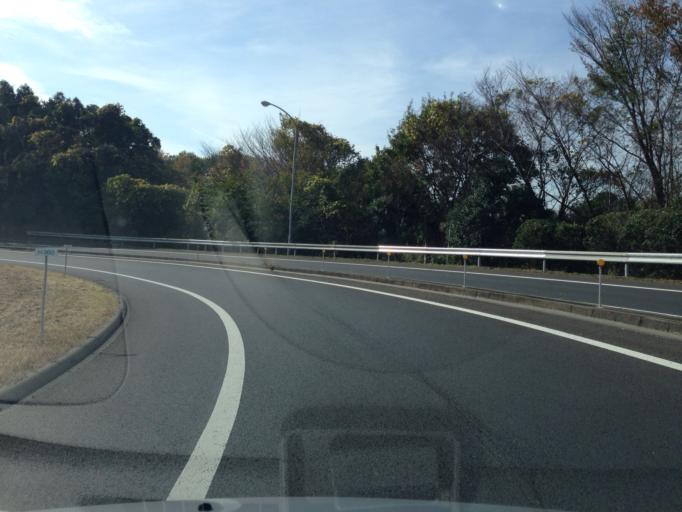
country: JP
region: Ibaraki
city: Naka
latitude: 36.0610
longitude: 140.1581
